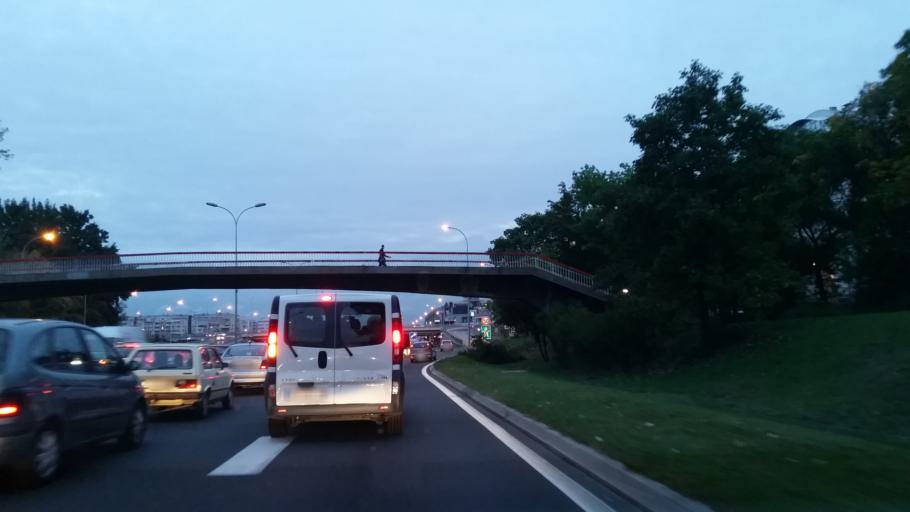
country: RS
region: Central Serbia
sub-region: Belgrade
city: Novi Beograd
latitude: 44.8146
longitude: 20.4154
